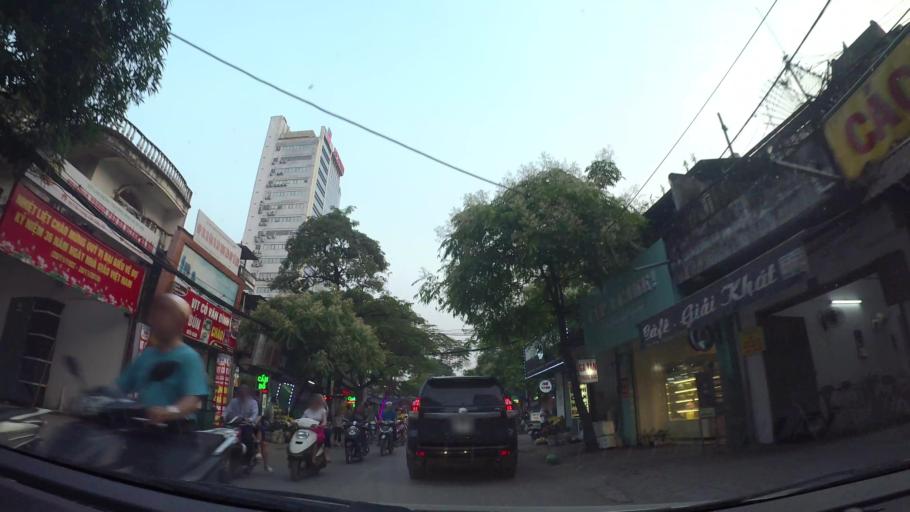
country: VN
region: Ha Noi
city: Cau Giay
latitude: 21.0475
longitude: 105.7901
